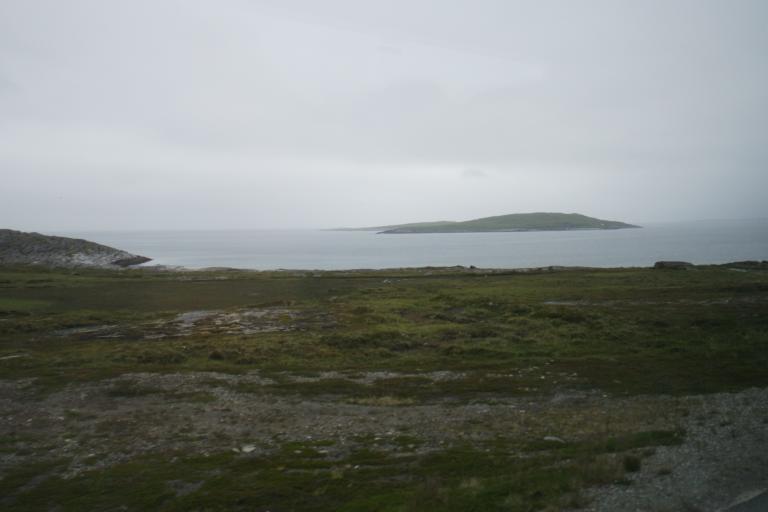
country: NO
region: Finnmark Fylke
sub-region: Nordkapp
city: Honningsvag
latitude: 70.8343
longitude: 25.7825
